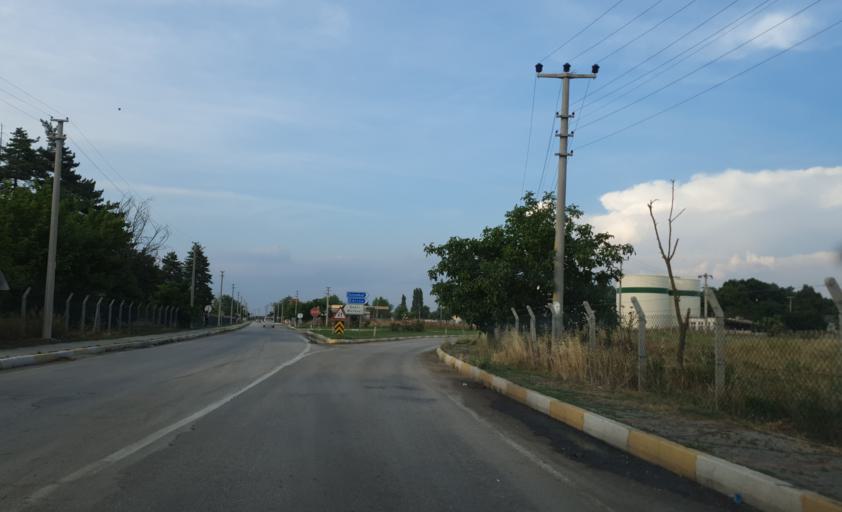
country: TR
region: Kirklareli
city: Babaeski
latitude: 41.3666
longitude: 27.1365
